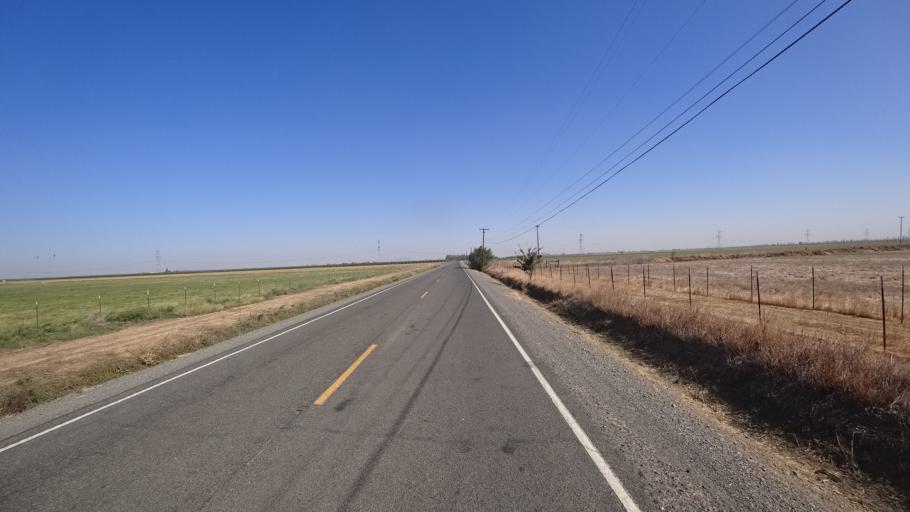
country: US
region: California
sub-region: Yolo County
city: Winters
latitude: 38.5837
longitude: -121.9214
